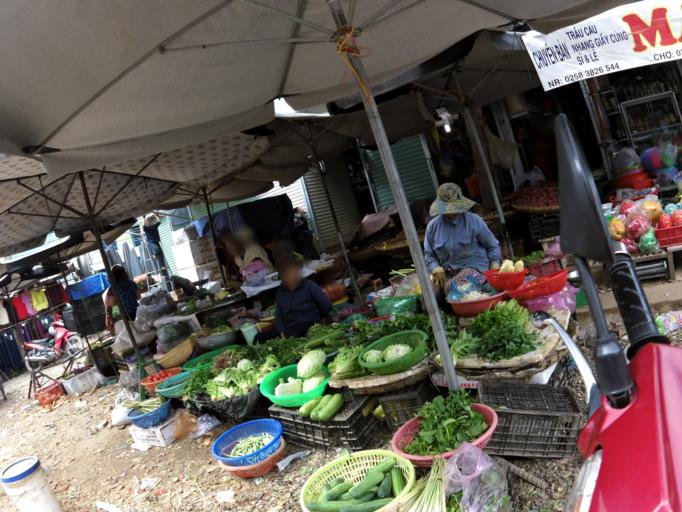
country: VN
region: Khanh Hoa
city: Nha Trang
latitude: 12.2557
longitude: 109.1912
